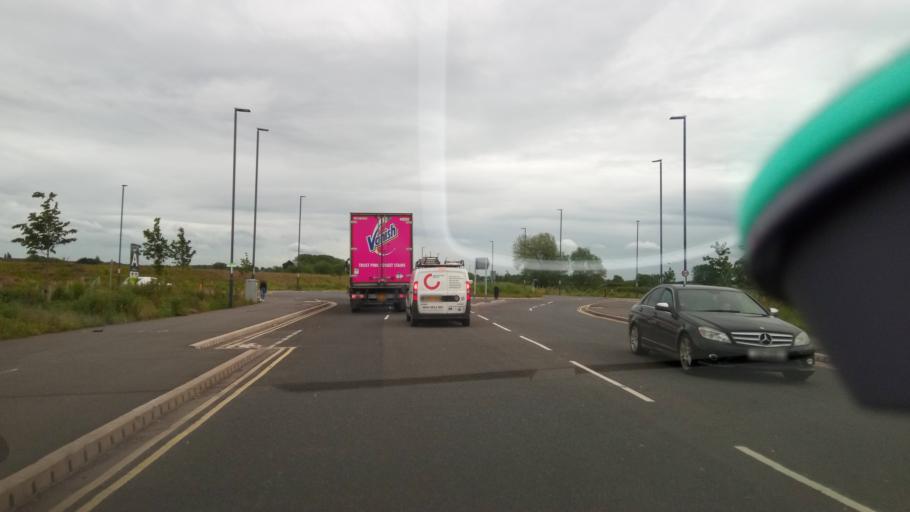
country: GB
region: England
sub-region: Derby
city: Derby
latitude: 52.8747
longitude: -1.4630
